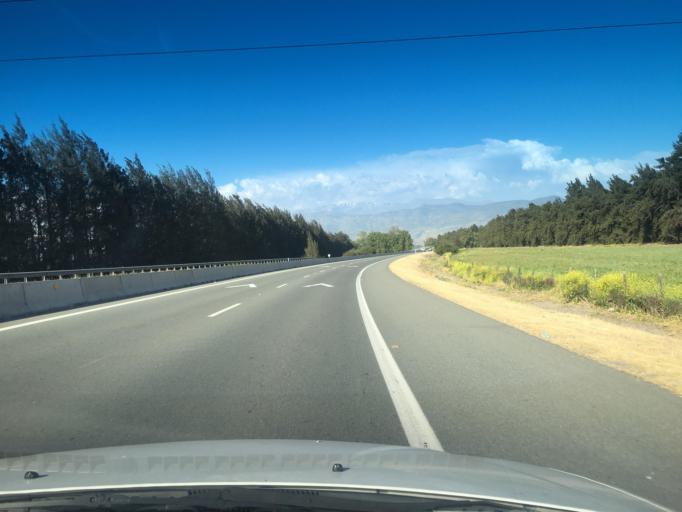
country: CL
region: Santiago Metropolitan
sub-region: Provincia de Chacabuco
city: Chicureo Abajo
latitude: -33.2945
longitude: -70.7189
